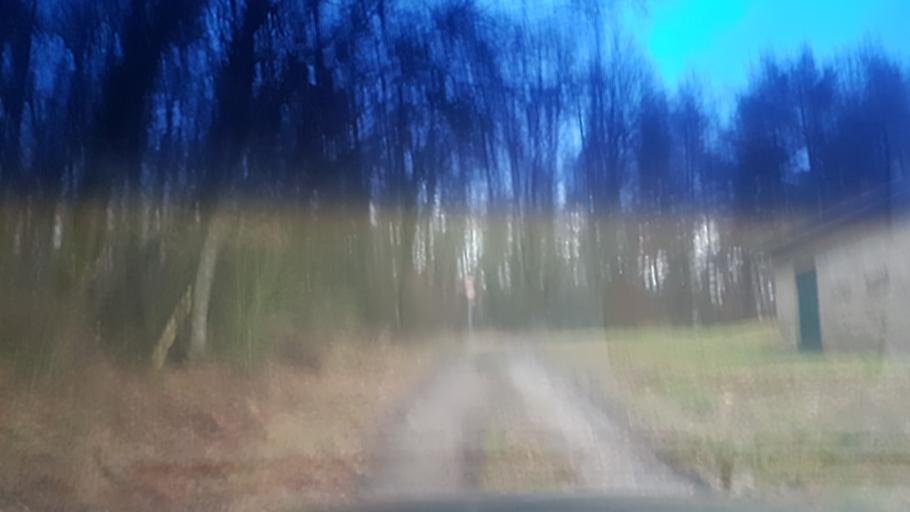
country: DE
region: Bavaria
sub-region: Upper Franconia
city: Zapfendorf
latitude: 50.0001
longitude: 10.9801
